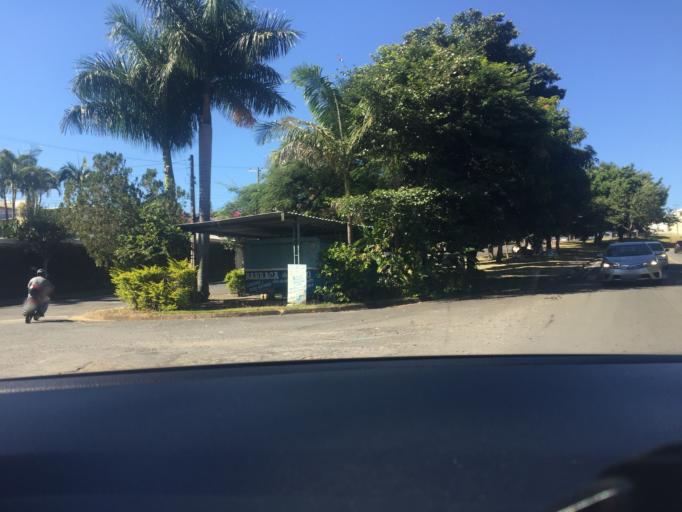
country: BR
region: Sao Paulo
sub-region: Santo Antonio Do Jardim
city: Espirito Santo do Pinhal
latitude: -22.1805
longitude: -46.7445
